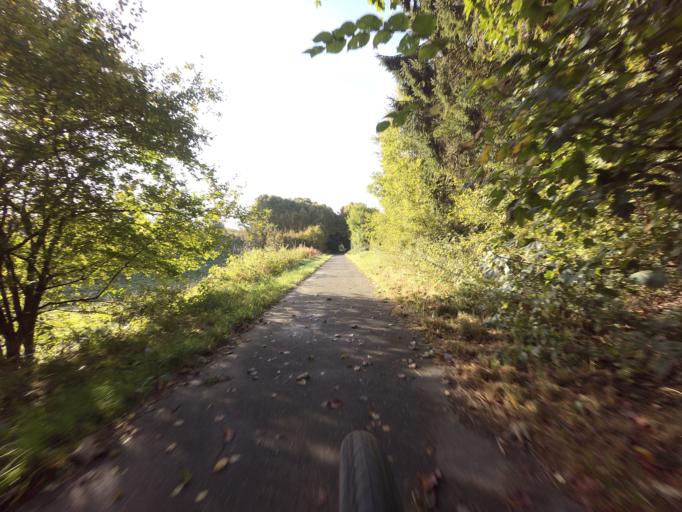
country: DK
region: Central Jutland
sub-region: Viborg Kommune
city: Bjerringbro
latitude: 56.4670
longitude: 9.5897
